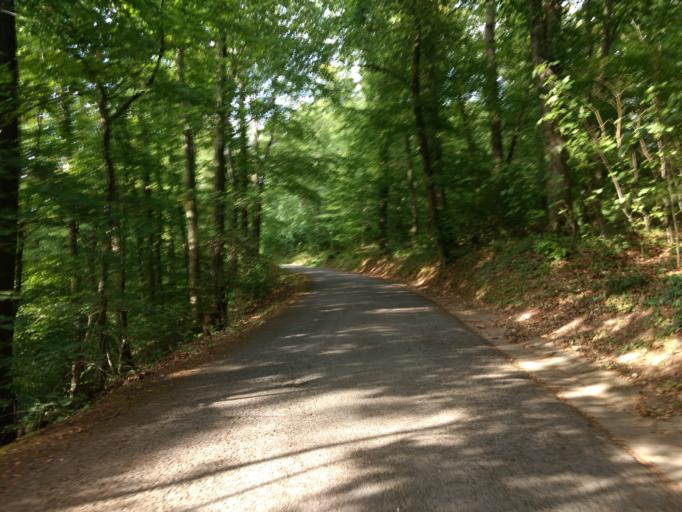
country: DE
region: Saarland
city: Rehlingen-Siersburg
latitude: 49.3388
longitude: 6.6835
